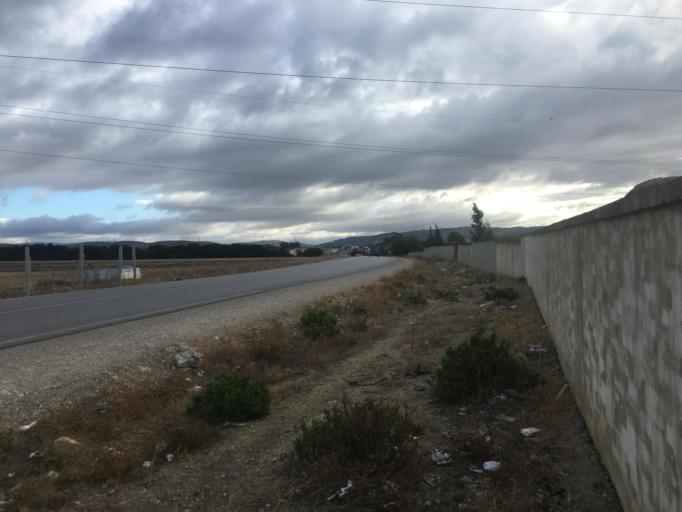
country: MA
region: Tanger-Tetouan
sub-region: Tanger-Assilah
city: Tangier
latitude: 35.6590
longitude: -5.7856
